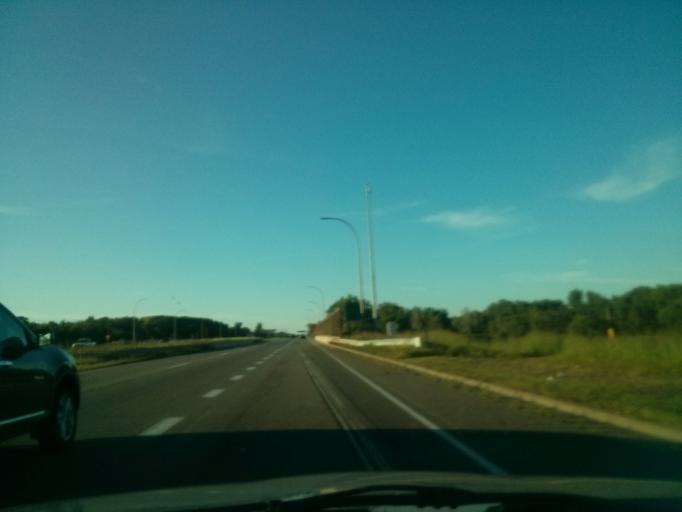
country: US
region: Minnesota
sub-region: Scott County
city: Savage
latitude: 44.8073
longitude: -93.3981
